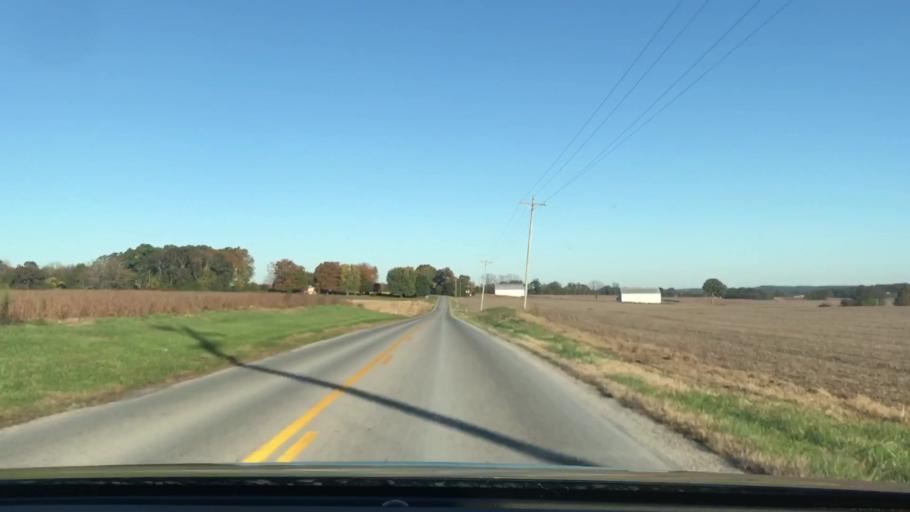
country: US
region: Kentucky
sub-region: Logan County
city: Auburn
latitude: 36.8412
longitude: -86.6938
